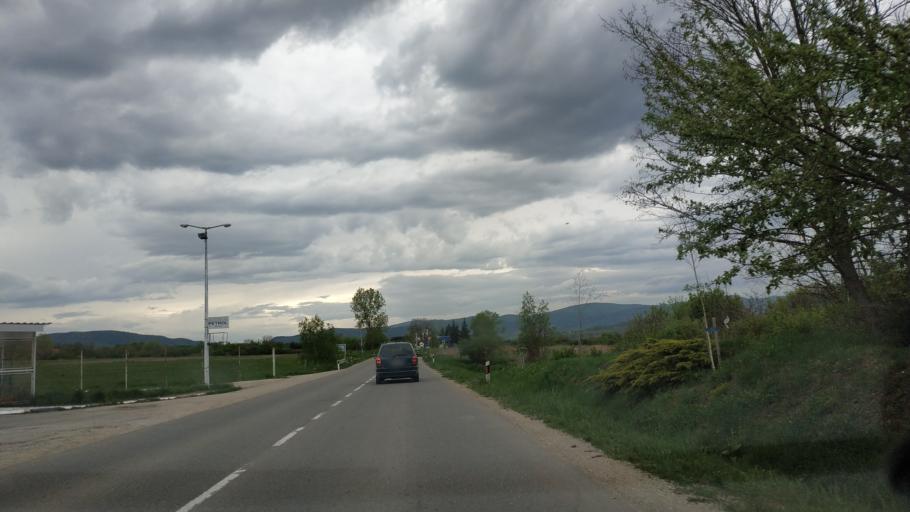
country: RS
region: Central Serbia
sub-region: Zajecarski Okrug
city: Soko Banja
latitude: 43.6524
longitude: 21.8461
